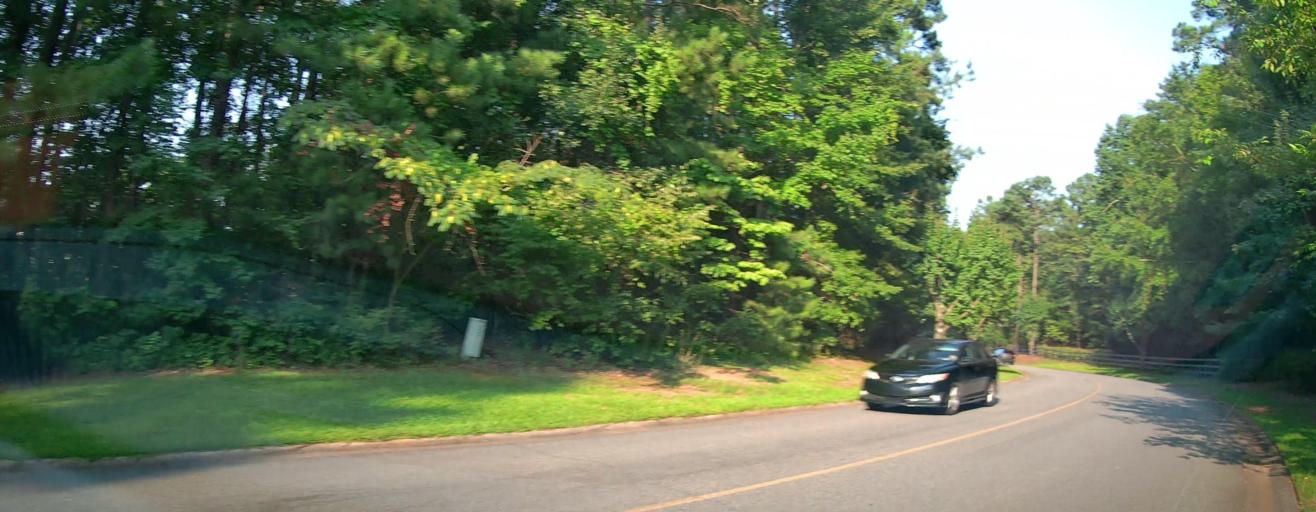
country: US
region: Georgia
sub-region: Bibb County
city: West Point
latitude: 32.8862
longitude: -83.7973
